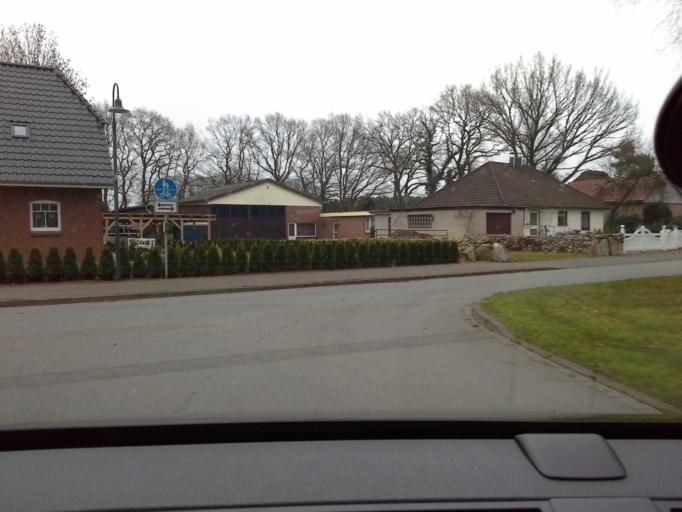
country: DE
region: Schleswig-Holstein
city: Lentfohrden
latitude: 53.8718
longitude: 9.8819
